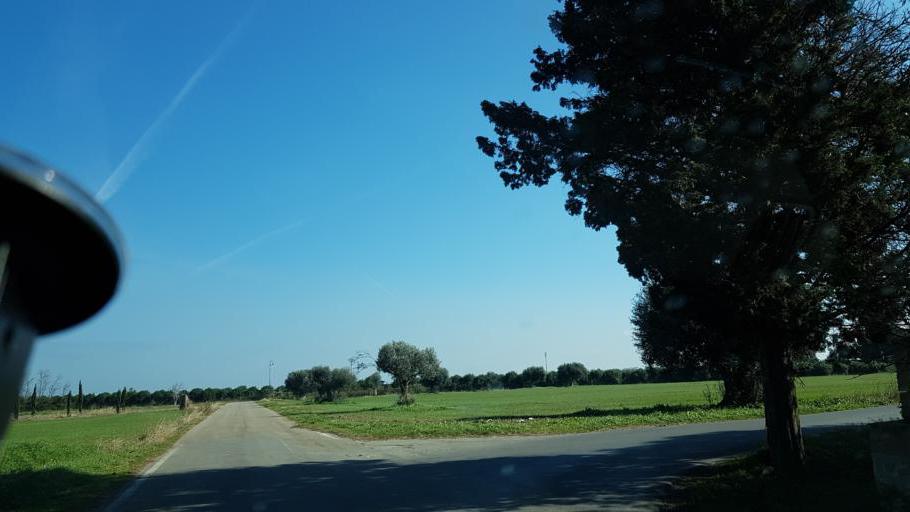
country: IT
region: Apulia
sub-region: Provincia di Brindisi
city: Brindisi
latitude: 40.6572
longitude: 17.9047
